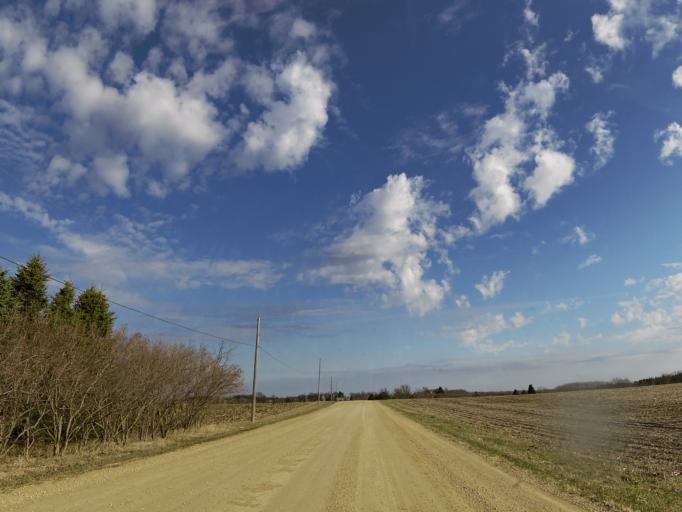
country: US
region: Minnesota
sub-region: Dakota County
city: Hastings
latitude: 44.8165
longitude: -92.8414
